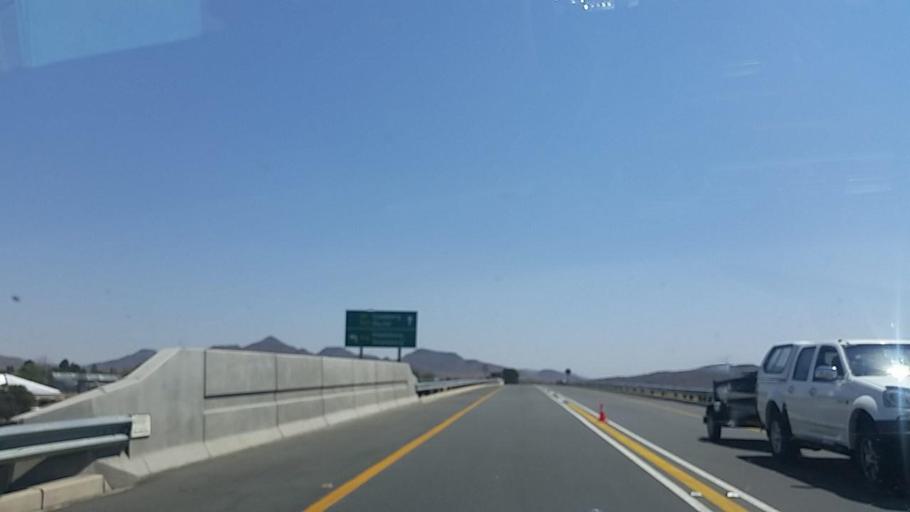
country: ZA
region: Eastern Cape
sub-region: Chris Hani District Municipality
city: Middelburg
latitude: -31.4951
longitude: 25.0178
